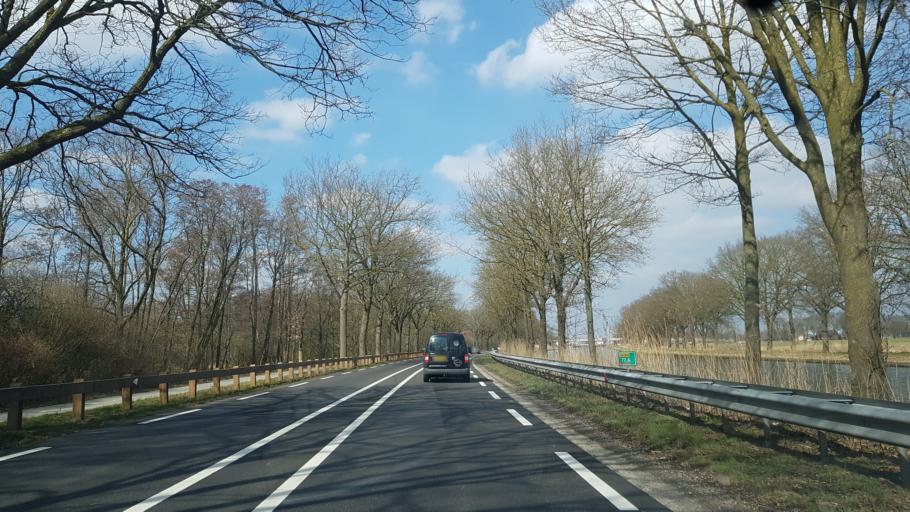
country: NL
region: North Brabant
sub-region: Gemeente Someren
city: Someren
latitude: 51.4110
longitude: 5.7034
